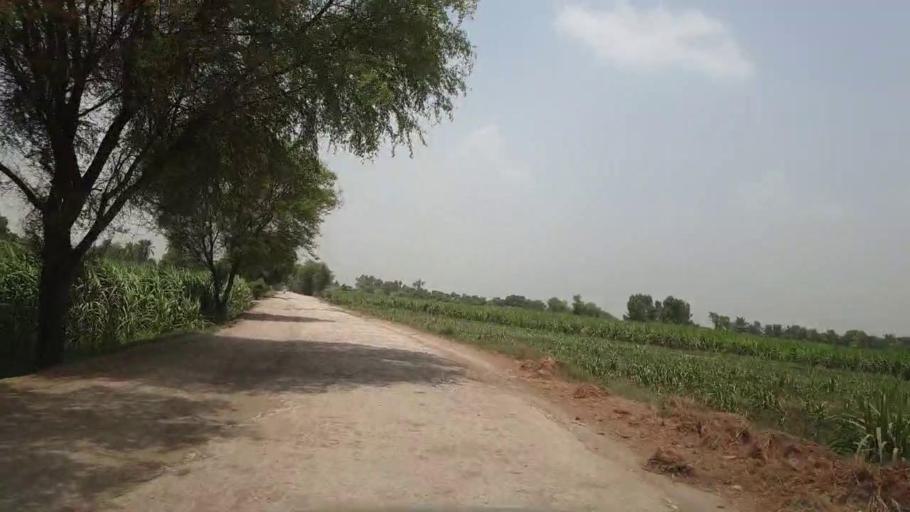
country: PK
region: Sindh
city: Sobhadero
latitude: 27.4375
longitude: 68.3967
